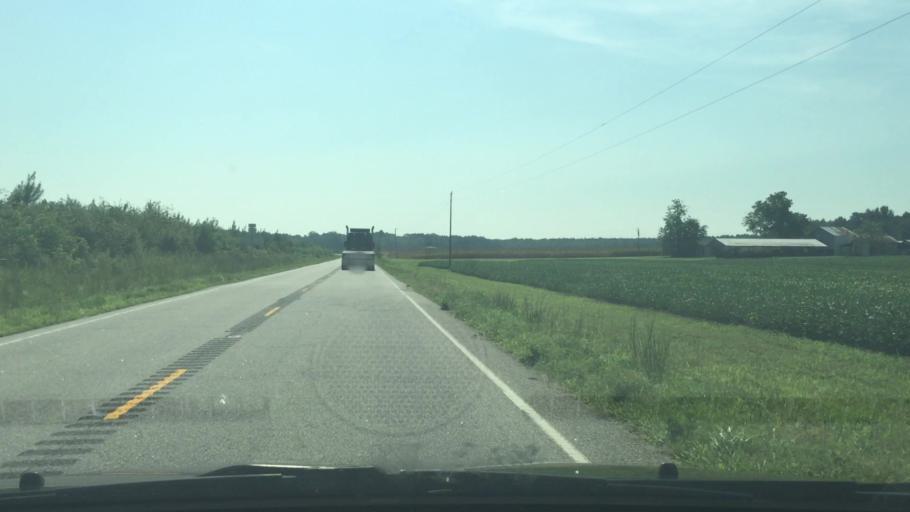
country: US
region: Virginia
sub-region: Sussex County
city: Sussex
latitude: 36.9790
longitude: -77.2308
